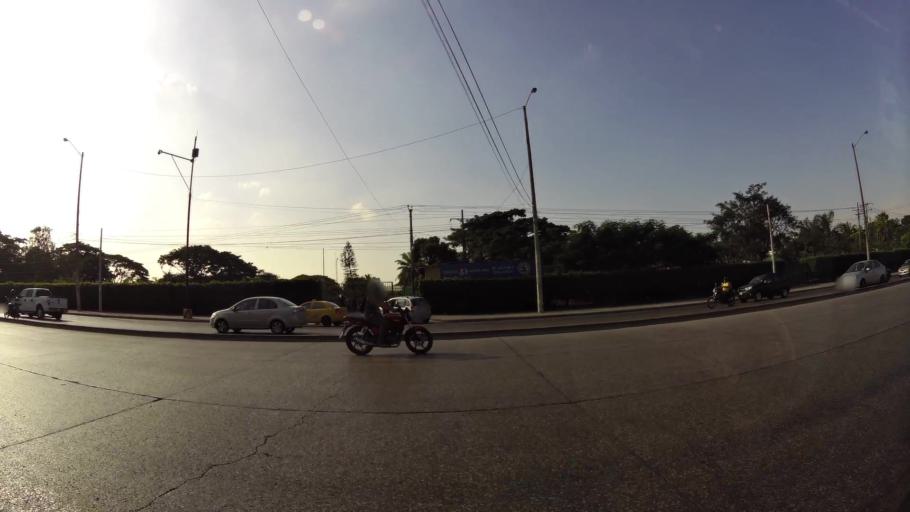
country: EC
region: Guayas
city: Guayaquil
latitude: -2.1402
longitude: -79.9304
